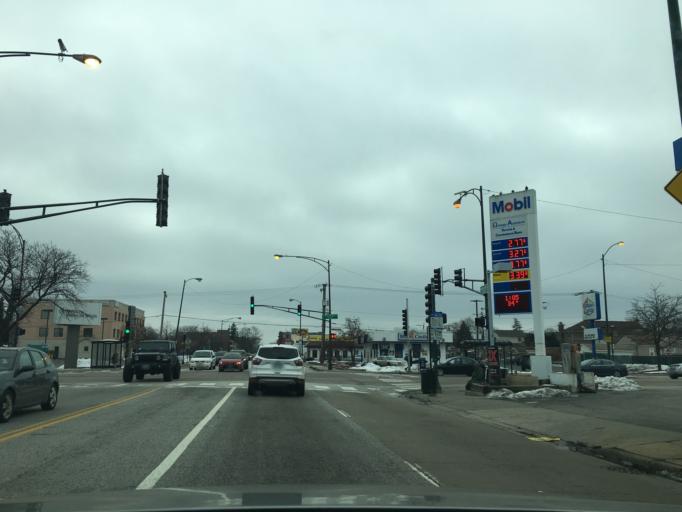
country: US
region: Illinois
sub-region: Cook County
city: Elmwood Park
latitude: 41.9384
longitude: -87.8068
